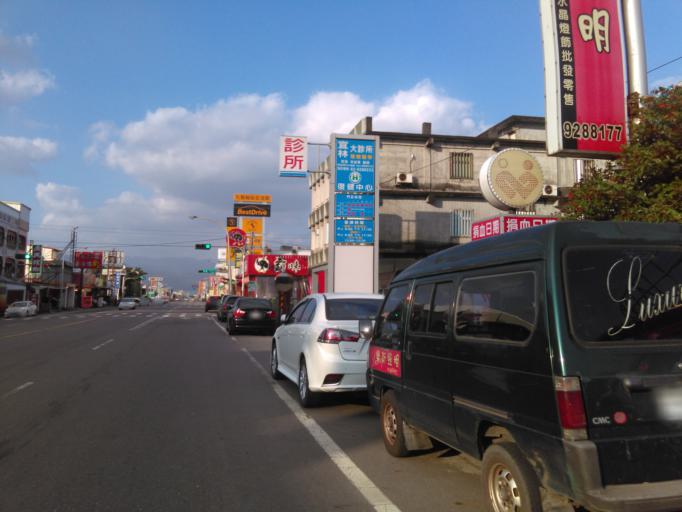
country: TW
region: Taiwan
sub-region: Yilan
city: Yilan
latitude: 24.7713
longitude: 121.7573
